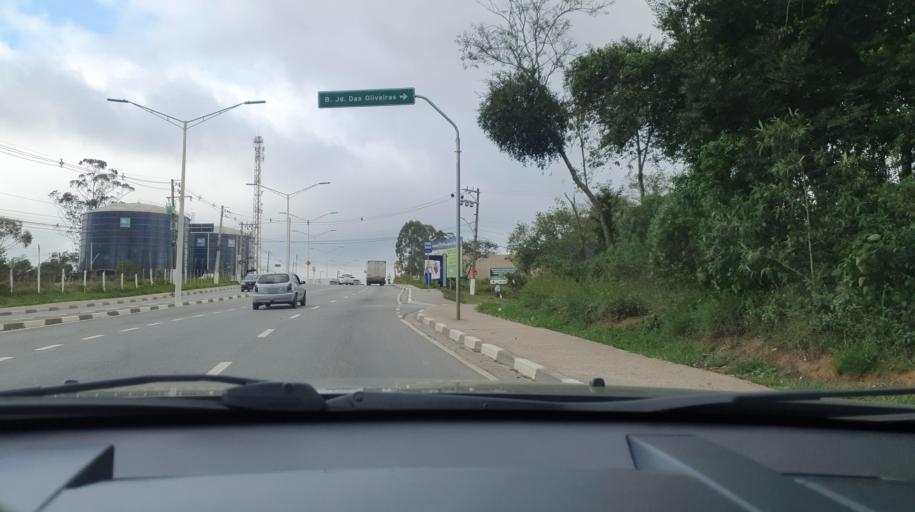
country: BR
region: Sao Paulo
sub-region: Vargem Grande Paulista
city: Vargem Grande Paulista
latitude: -23.6748
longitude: -47.0152
